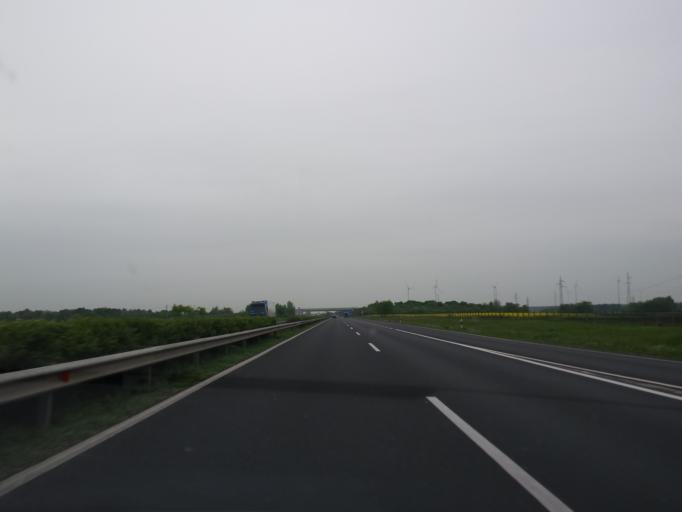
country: HU
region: Gyor-Moson-Sopron
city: Mosonmagyarovar
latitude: 47.8548
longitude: 17.2444
